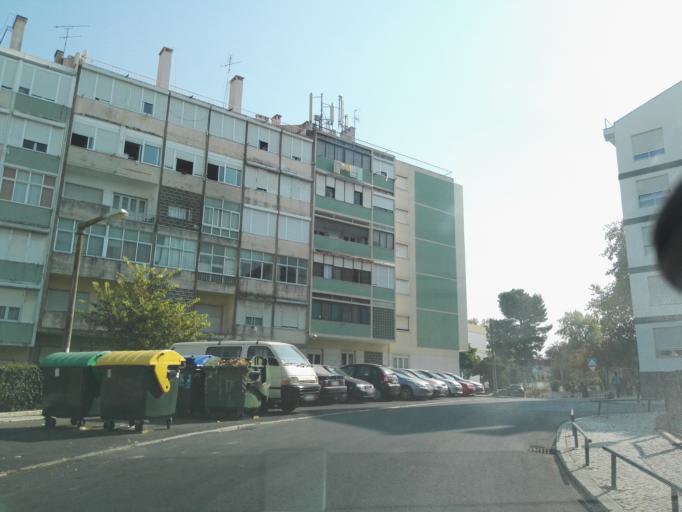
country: PT
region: Lisbon
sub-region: Lisbon
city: Lisbon
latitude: 38.7353
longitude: -9.1141
